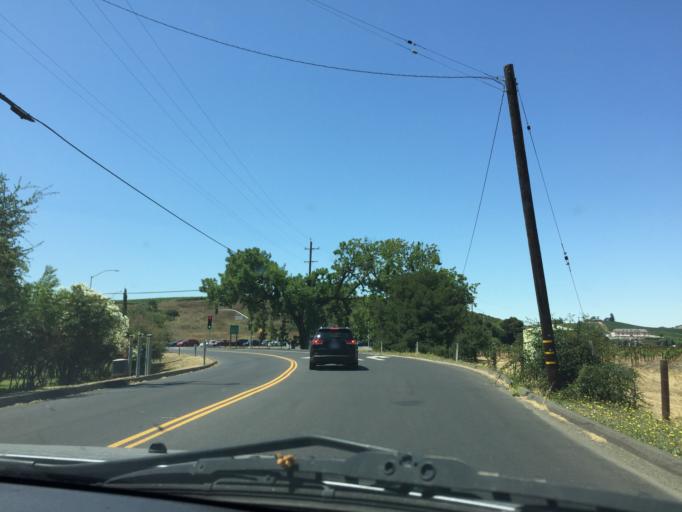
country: US
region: California
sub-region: Napa County
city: Napa
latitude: 38.2562
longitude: -122.3417
